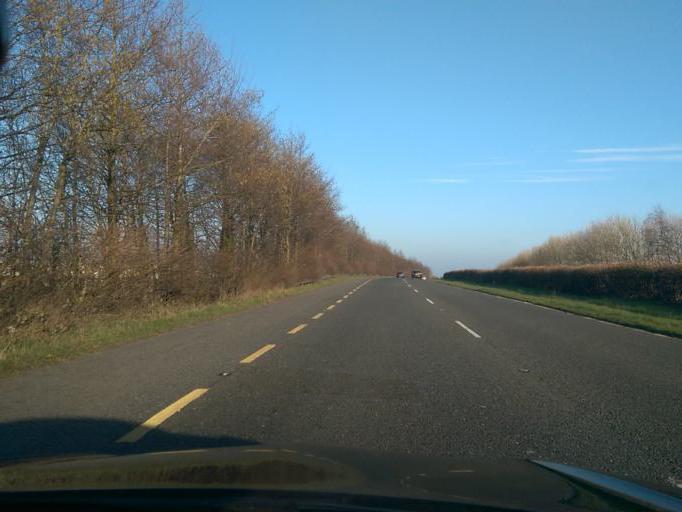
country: IE
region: Connaught
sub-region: County Galway
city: Oranmore
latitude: 53.2783
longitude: -8.9426
